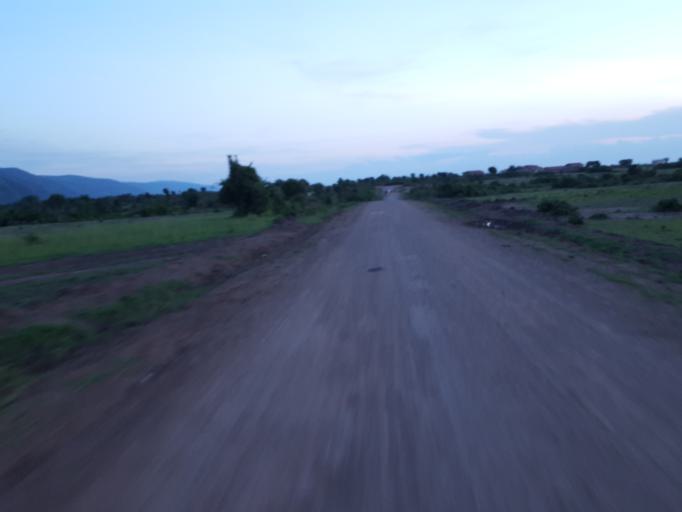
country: UG
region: Western Region
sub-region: Kibale District
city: Kagadi
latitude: 1.2394
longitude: 30.7456
